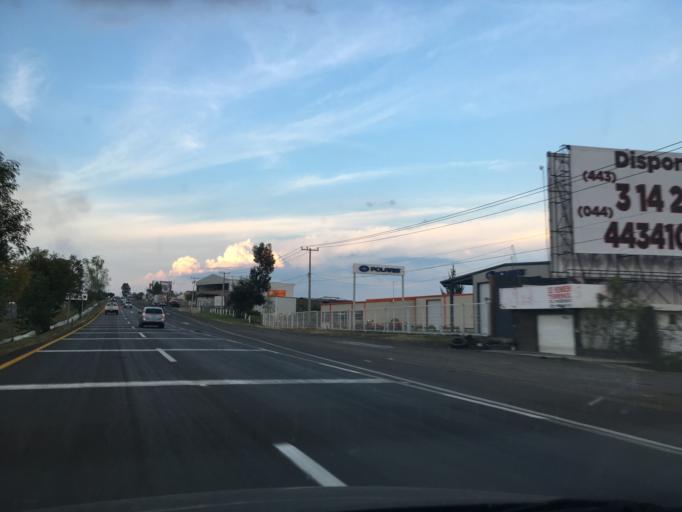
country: MX
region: Michoacan
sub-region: Morelia
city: La Mintzita (Piedra Dura)
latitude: 19.6212
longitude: -101.2805
